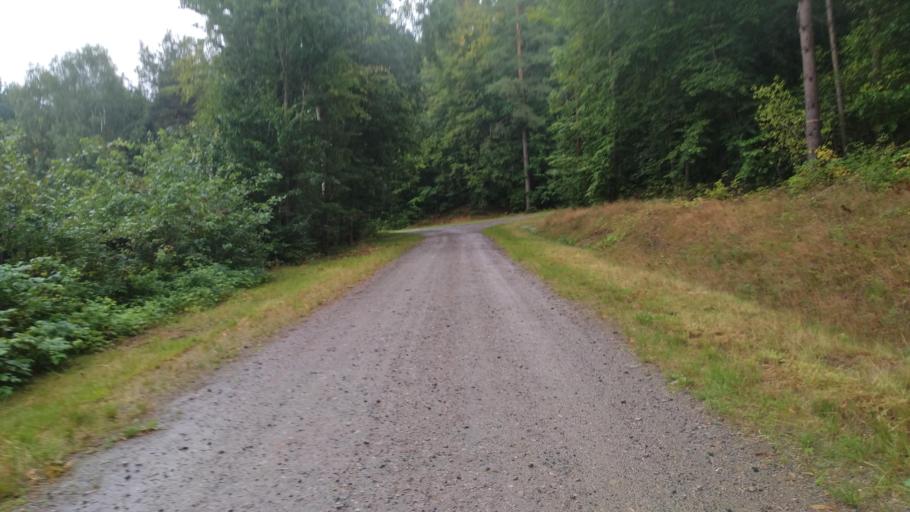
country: PL
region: Pomeranian Voivodeship
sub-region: Powiat wejherowski
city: Goscicino
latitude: 54.6277
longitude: 18.1404
